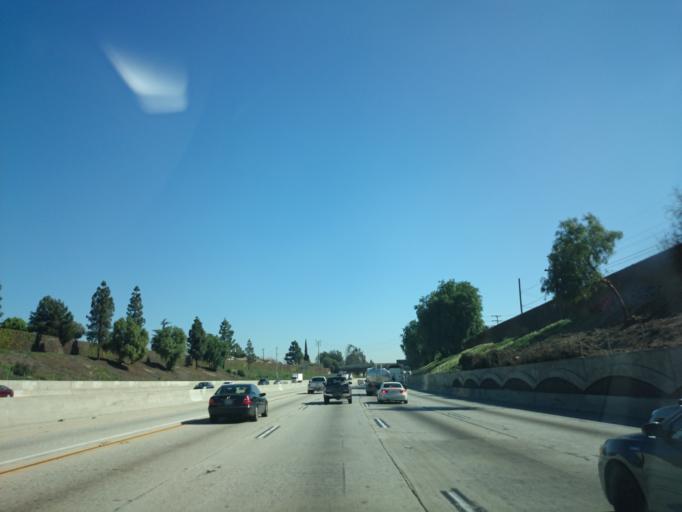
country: US
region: California
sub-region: San Bernardino County
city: Upland
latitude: 34.0865
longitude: -117.6399
